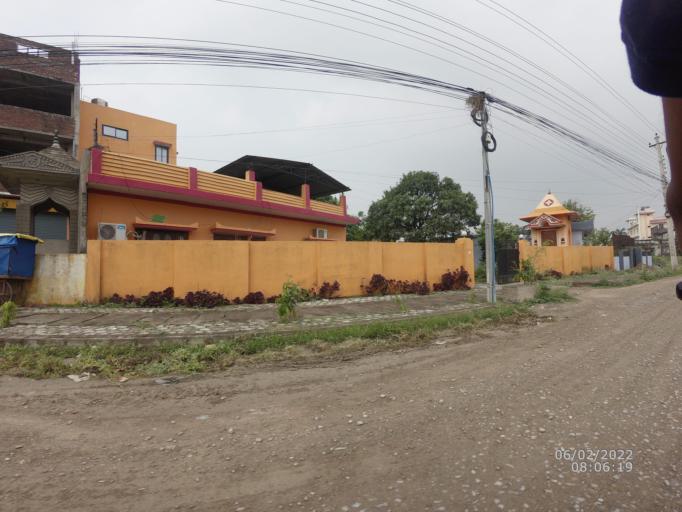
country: NP
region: Western Region
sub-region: Lumbini Zone
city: Bhairahawa
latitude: 27.4798
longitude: 83.4670
